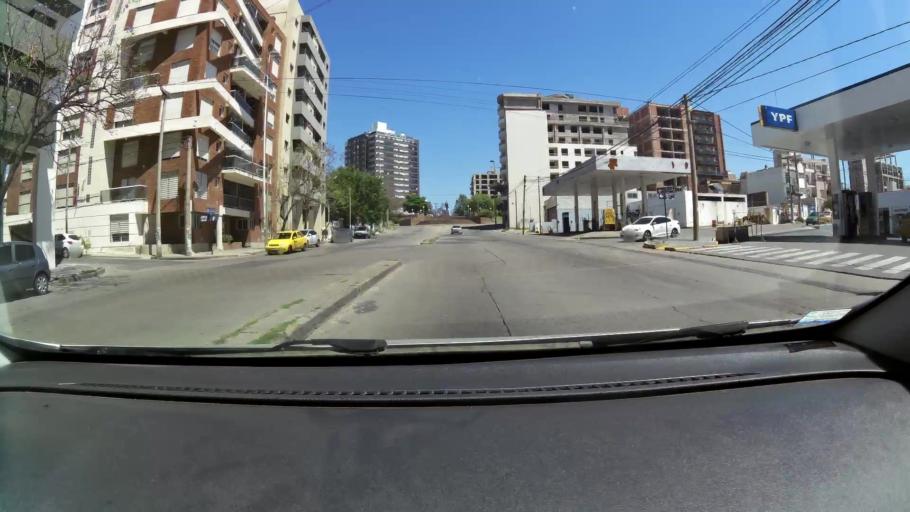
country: AR
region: Cordoba
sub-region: Departamento de Capital
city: Cordoba
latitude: -31.4243
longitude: -64.1987
